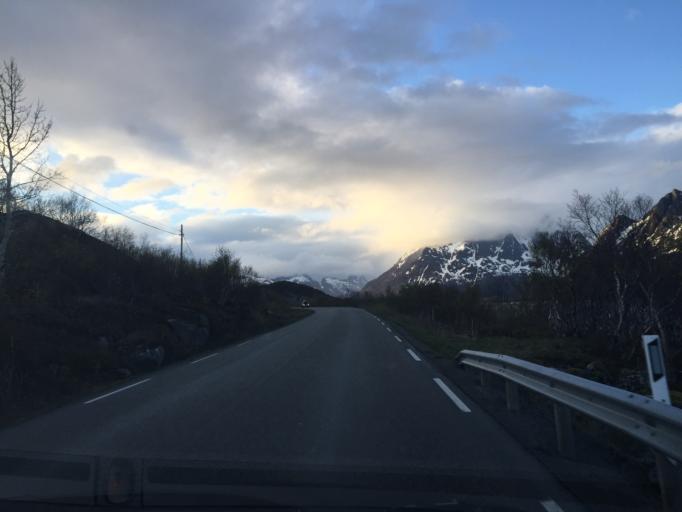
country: NO
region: Nordland
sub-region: Vagan
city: Svolvaer
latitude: 68.2891
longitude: 14.6958
